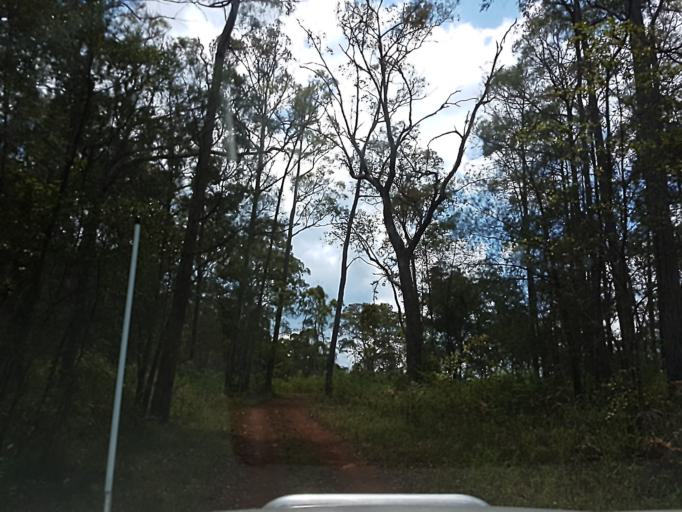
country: AU
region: Victoria
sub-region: East Gippsland
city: Lakes Entrance
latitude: -37.3486
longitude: 148.3576
